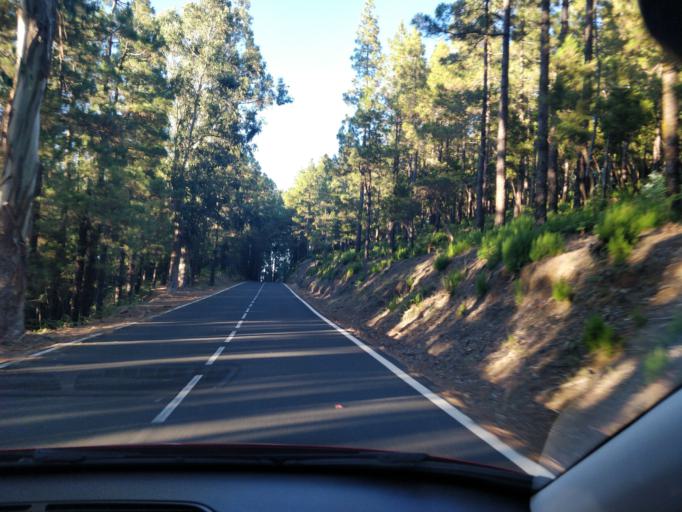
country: ES
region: Canary Islands
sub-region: Provincia de Santa Cruz de Tenerife
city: La Victoria de Acentejo
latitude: 28.4082
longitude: -16.4227
